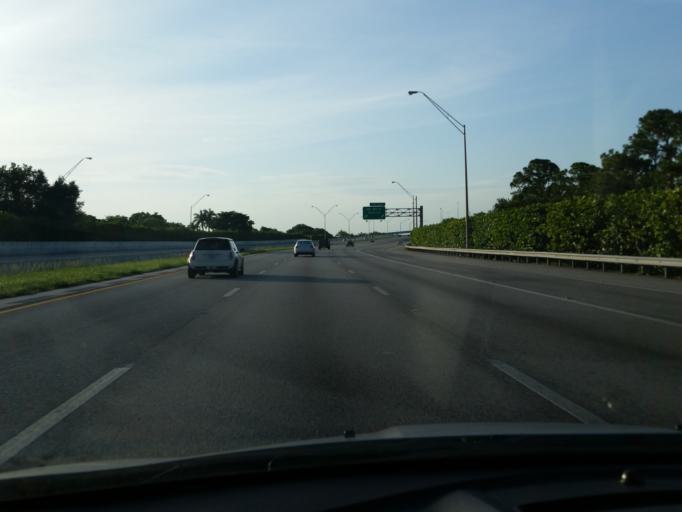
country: US
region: Florida
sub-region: Miami-Dade County
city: Scott Lake
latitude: 25.9488
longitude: -80.2275
